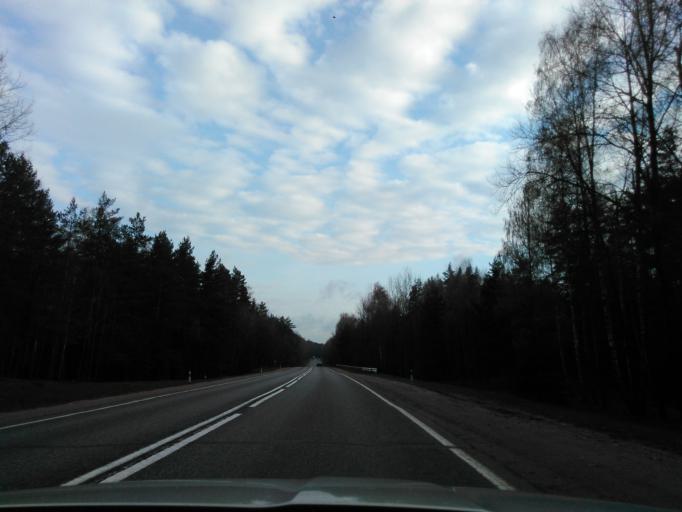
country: BY
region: Minsk
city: Lahoysk
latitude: 54.3183
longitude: 27.8753
